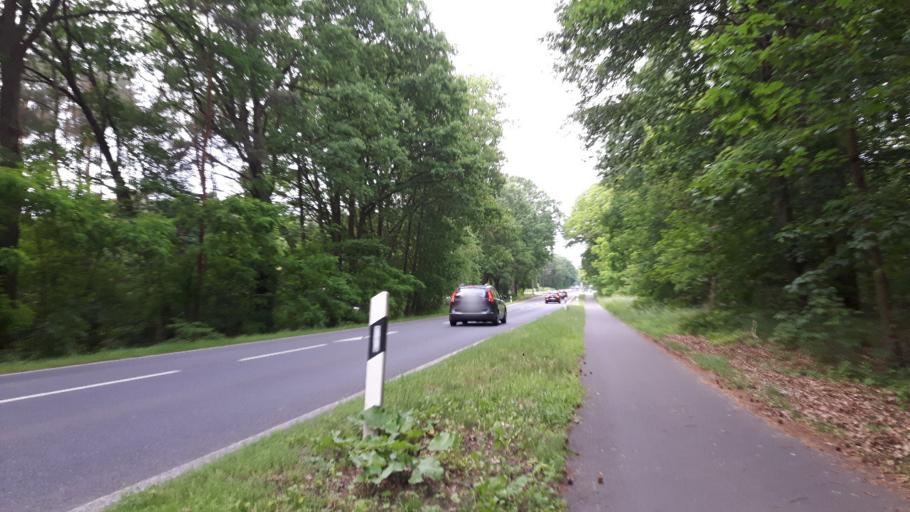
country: DE
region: Brandenburg
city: Michendorf
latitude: 52.3531
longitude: 13.0443
